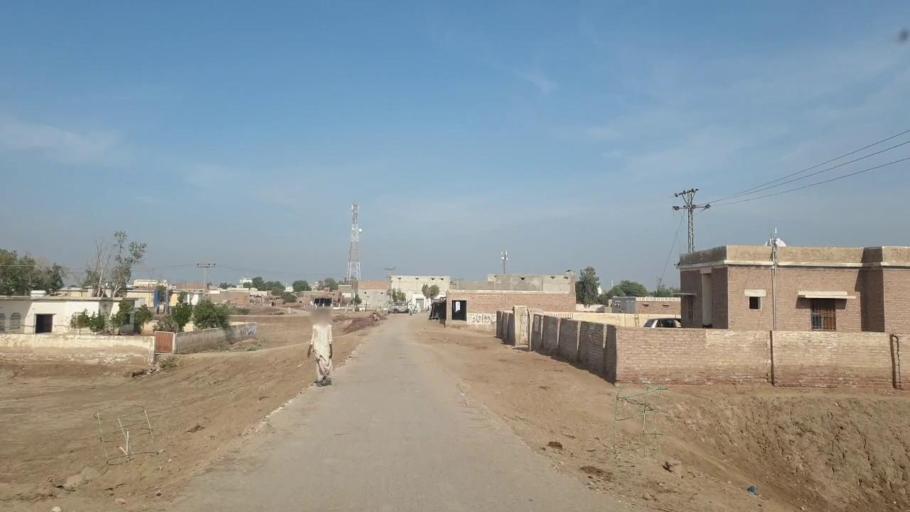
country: PK
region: Sindh
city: Sann
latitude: 25.9055
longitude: 68.2334
